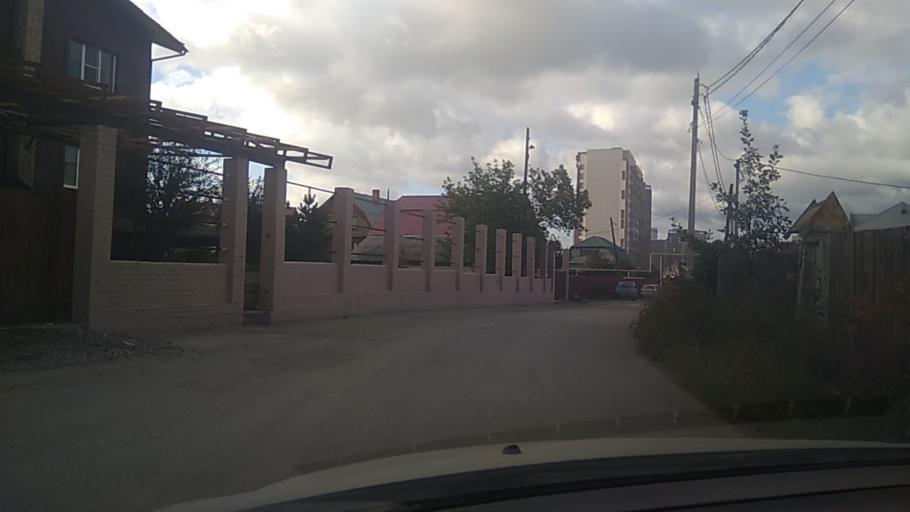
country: RU
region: Sverdlovsk
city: Shirokaya Rechka
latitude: 56.8027
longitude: 60.5023
